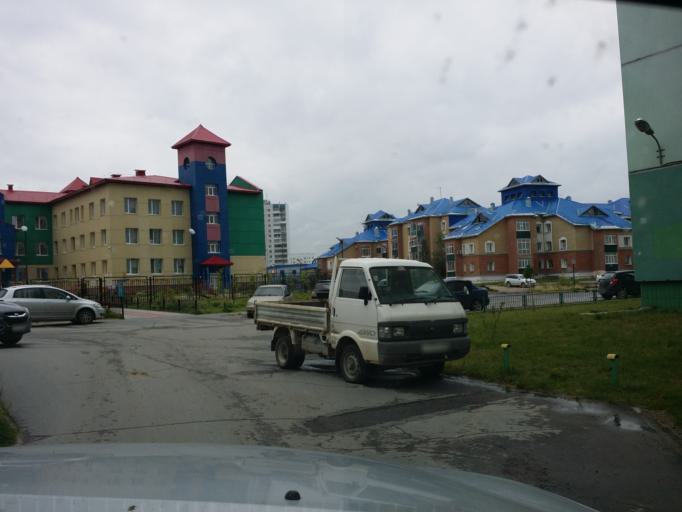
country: RU
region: Khanty-Mansiyskiy Avtonomnyy Okrug
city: Nizhnevartovsk
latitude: 60.9574
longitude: 76.5772
